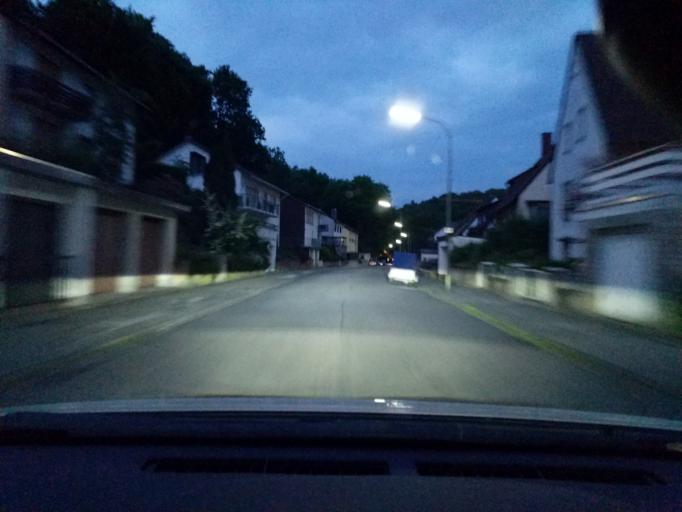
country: DE
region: Rheinland-Pfalz
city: Kaiserslautern
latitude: 49.4501
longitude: 7.7445
